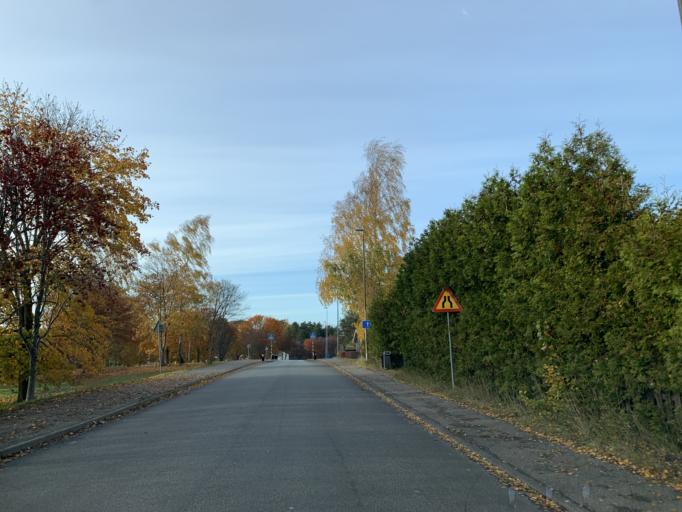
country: SE
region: Stockholm
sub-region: Haninge Kommun
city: Haninge
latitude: 59.1755
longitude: 18.1848
